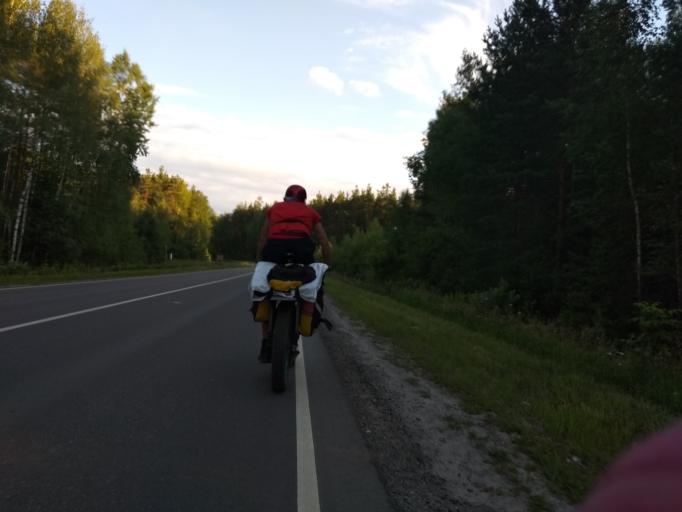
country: RU
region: Moskovskaya
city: Misheronskiy
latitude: 55.7100
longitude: 39.7400
